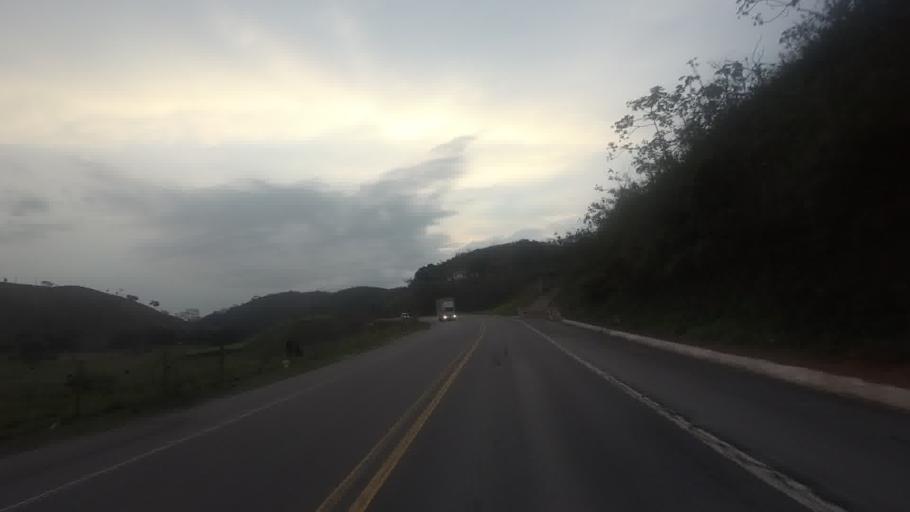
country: BR
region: Minas Gerais
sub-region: Alem Paraiba
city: Alem Paraiba
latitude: -21.8413
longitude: -42.6235
